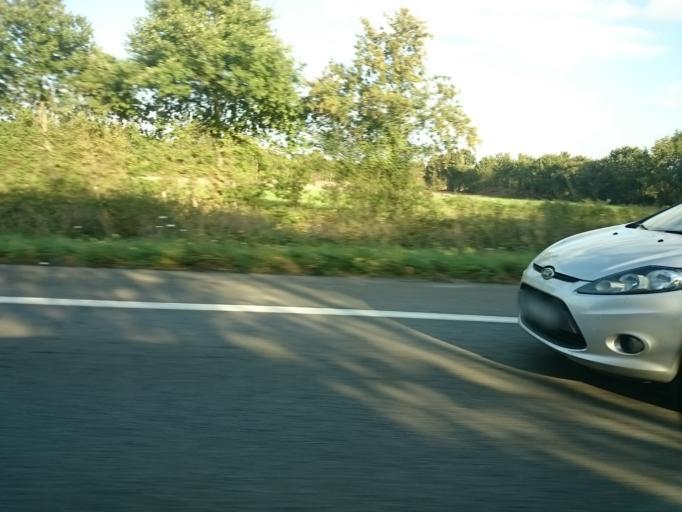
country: FR
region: Pays de la Loire
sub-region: Departement de la Loire-Atlantique
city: Heric
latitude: 47.3822
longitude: -1.6429
